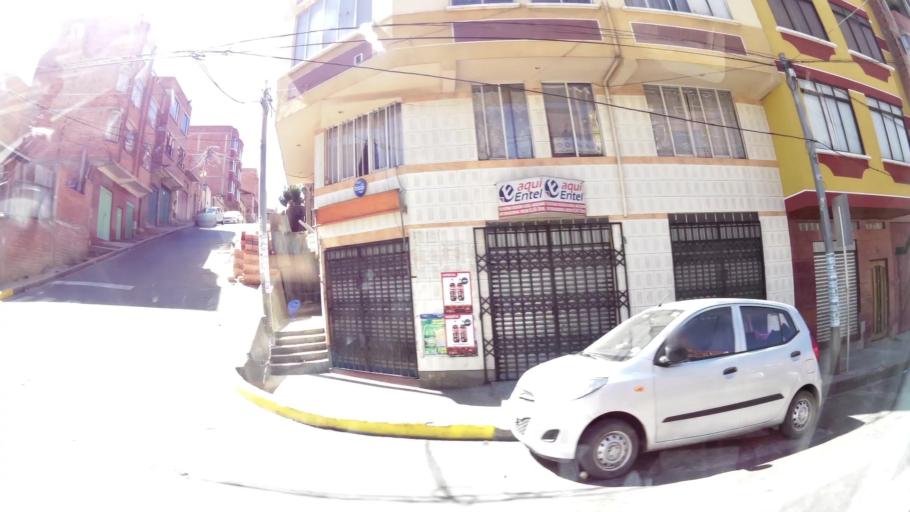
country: BO
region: La Paz
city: La Paz
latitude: -16.4925
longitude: -68.1524
